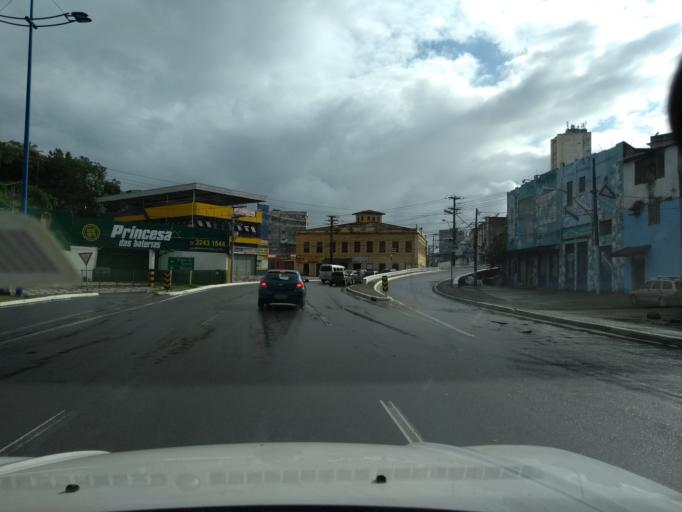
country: BR
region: Bahia
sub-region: Salvador
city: Salvador
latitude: -12.9768
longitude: -38.5013
